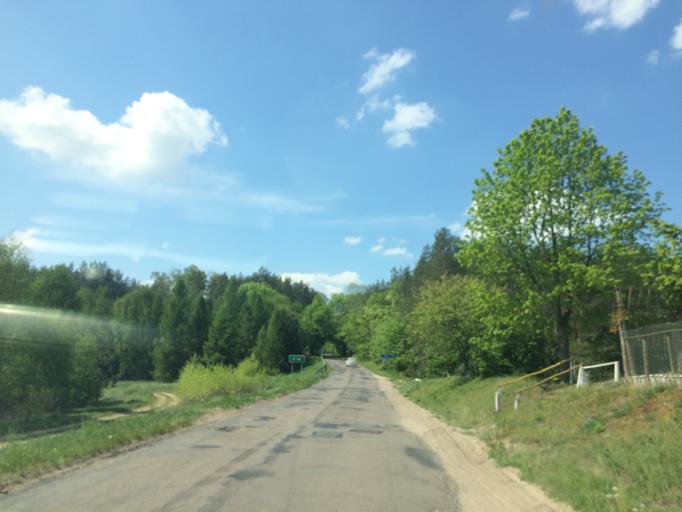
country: PL
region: Warmian-Masurian Voivodeship
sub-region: Powiat nowomiejski
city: Nowe Miasto Lubawskie
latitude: 53.4265
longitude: 19.6853
